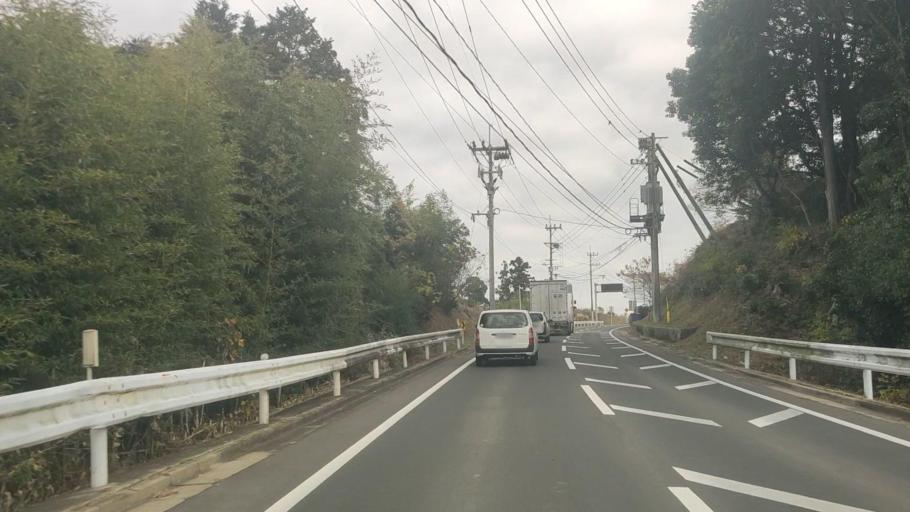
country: JP
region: Nagasaki
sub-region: Isahaya-shi
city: Isahaya
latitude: 32.8159
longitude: 130.1738
